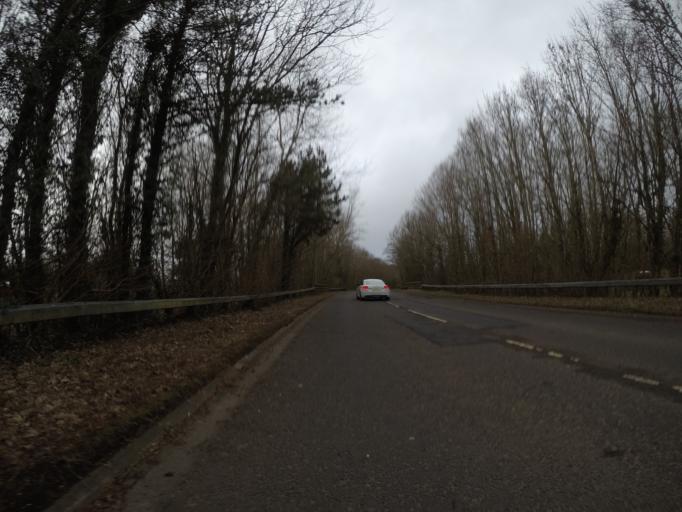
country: GB
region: Scotland
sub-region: North Ayrshire
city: Irvine
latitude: 55.6307
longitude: -4.6318
